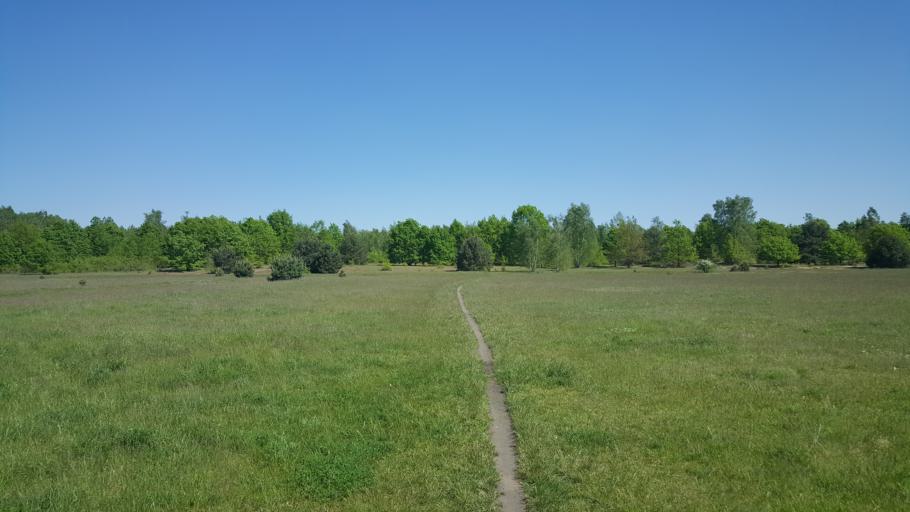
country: DE
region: Saxony
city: Albertstadt
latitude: 51.0972
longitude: 13.7476
